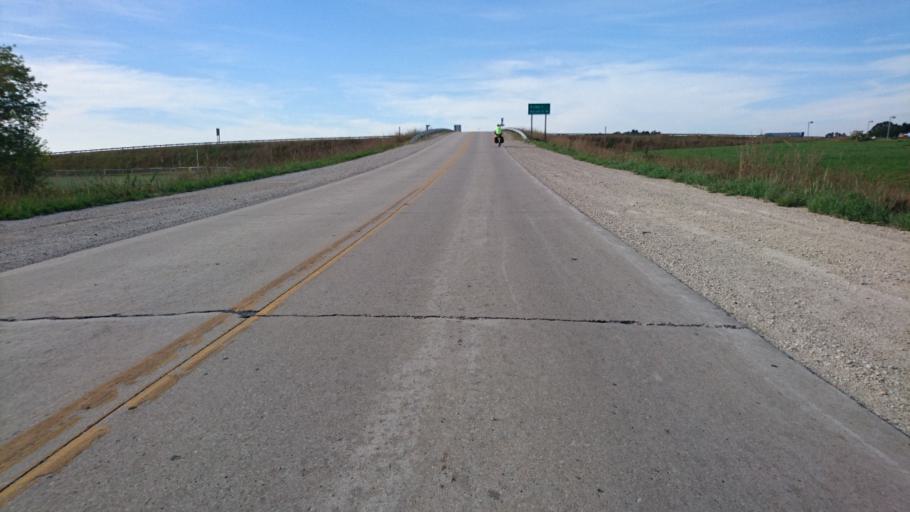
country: US
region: Missouri
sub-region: Crawford County
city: Cuba
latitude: 38.0917
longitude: -91.3668
